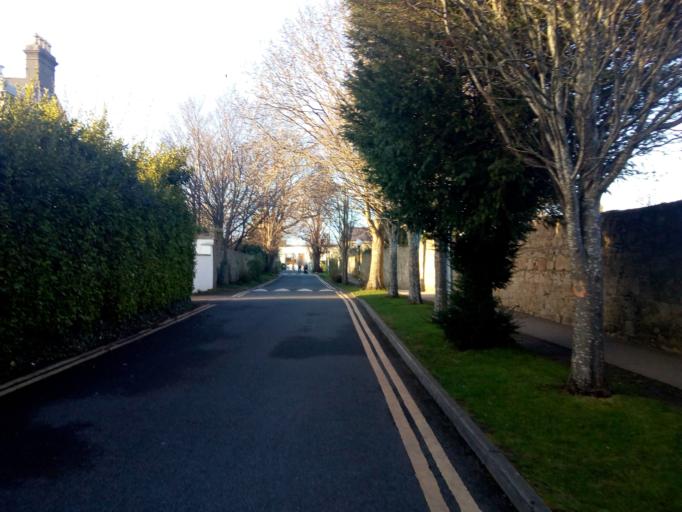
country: IE
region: Leinster
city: Sallynoggin
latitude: 53.2866
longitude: -6.1389
